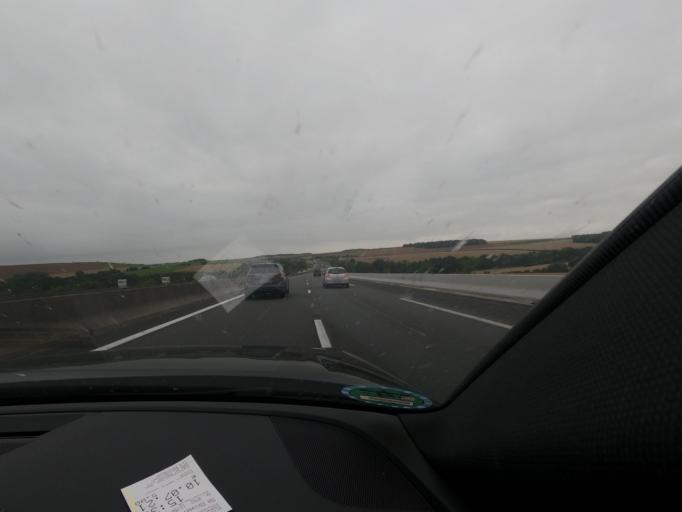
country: FR
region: Picardie
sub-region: Departement de la Somme
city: Cagny
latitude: 49.8564
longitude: 2.3194
